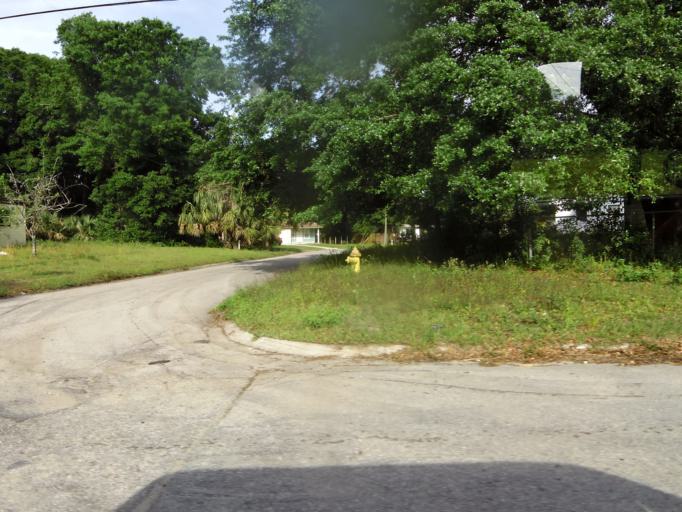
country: US
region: Florida
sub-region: Duval County
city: Jacksonville
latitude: 30.3372
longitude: -81.5866
